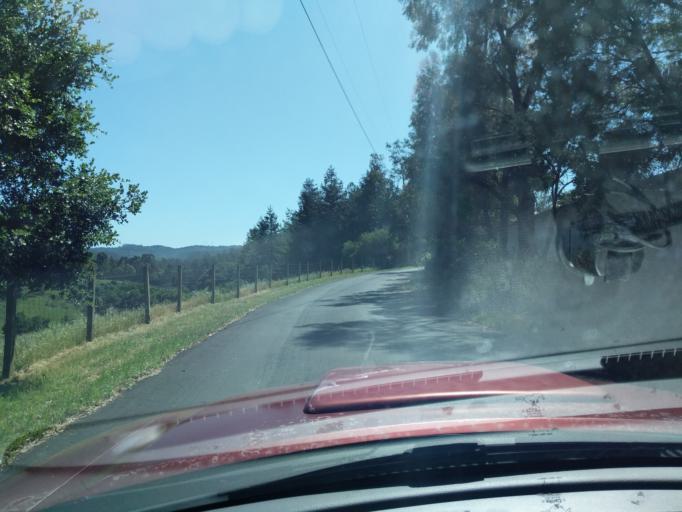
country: US
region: California
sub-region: San Benito County
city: Aromas
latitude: 36.8696
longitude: -121.6866
